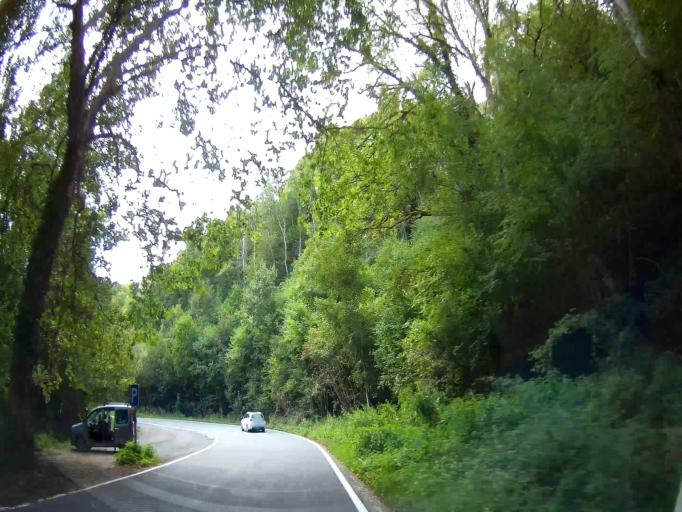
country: BE
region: Wallonia
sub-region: Province de Namur
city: Onhaye
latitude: 50.2941
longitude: 4.8124
